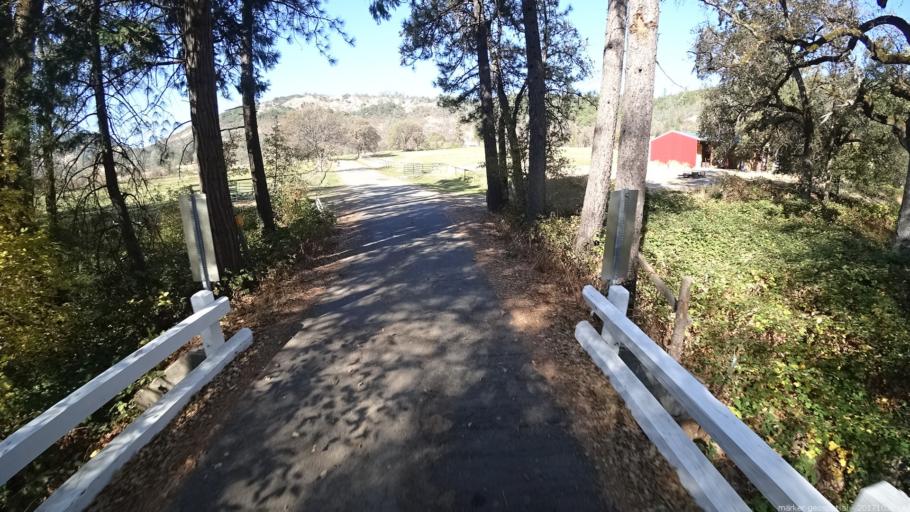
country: US
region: California
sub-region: Shasta County
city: Shingletown
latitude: 40.5691
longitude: -121.8801
